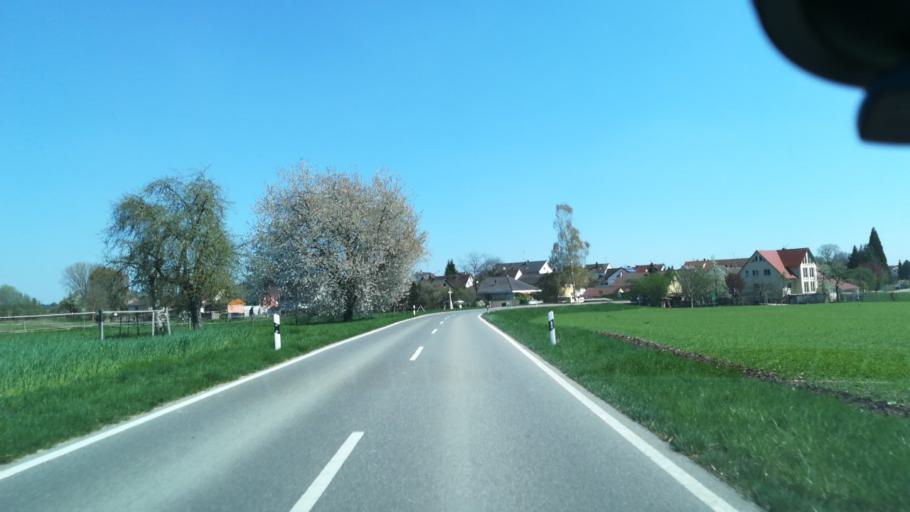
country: DE
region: Baden-Wuerttemberg
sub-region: Freiburg Region
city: Neuhausen
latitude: 47.8288
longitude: 8.7951
